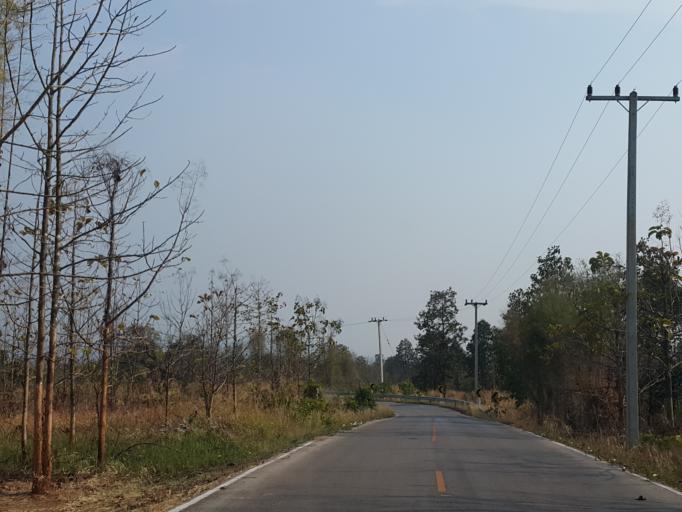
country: TH
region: Lampang
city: Chae Hom
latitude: 18.7269
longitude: 99.5540
